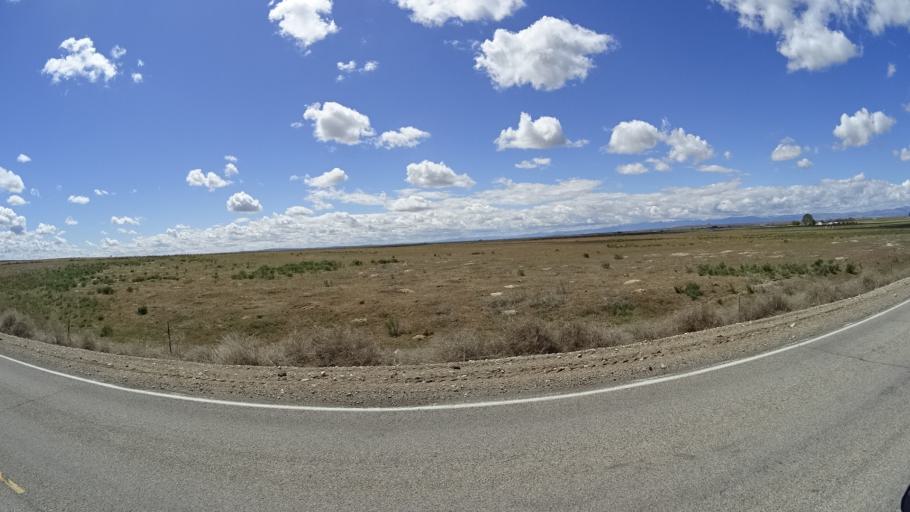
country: US
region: Idaho
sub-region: Ada County
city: Kuna
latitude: 43.4593
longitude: -116.3057
